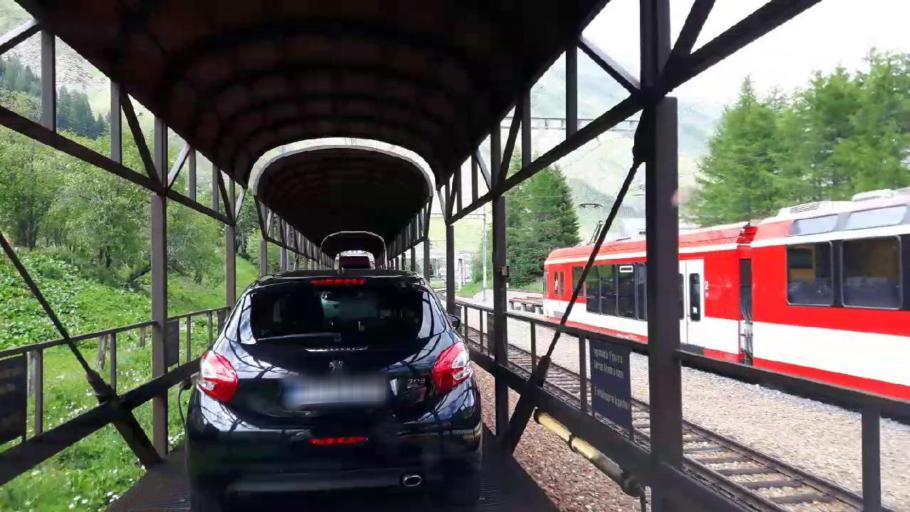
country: CH
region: Uri
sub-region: Uri
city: Andermatt
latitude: 46.5955
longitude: 8.5016
